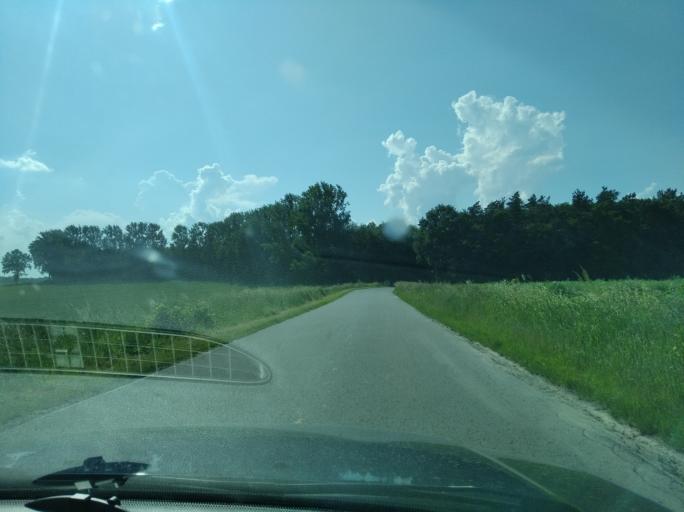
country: PL
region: Subcarpathian Voivodeship
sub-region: Powiat jaroslawski
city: Rokietnica
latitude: 49.9282
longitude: 22.6799
